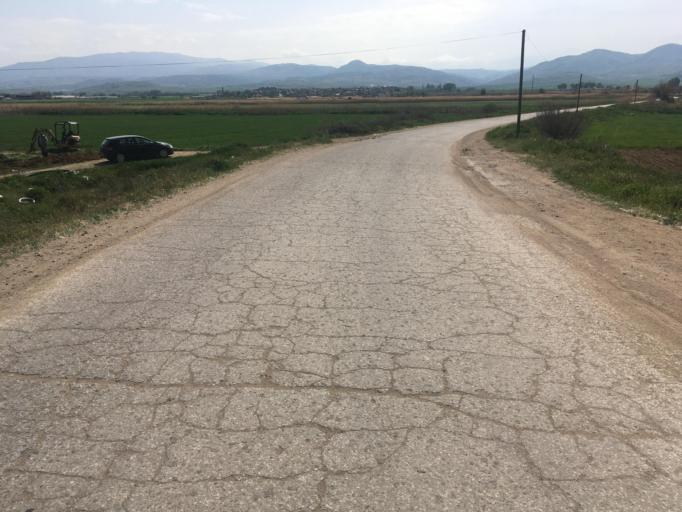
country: MK
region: Karbinci
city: Karbinci
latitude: 41.8039
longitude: 22.2074
